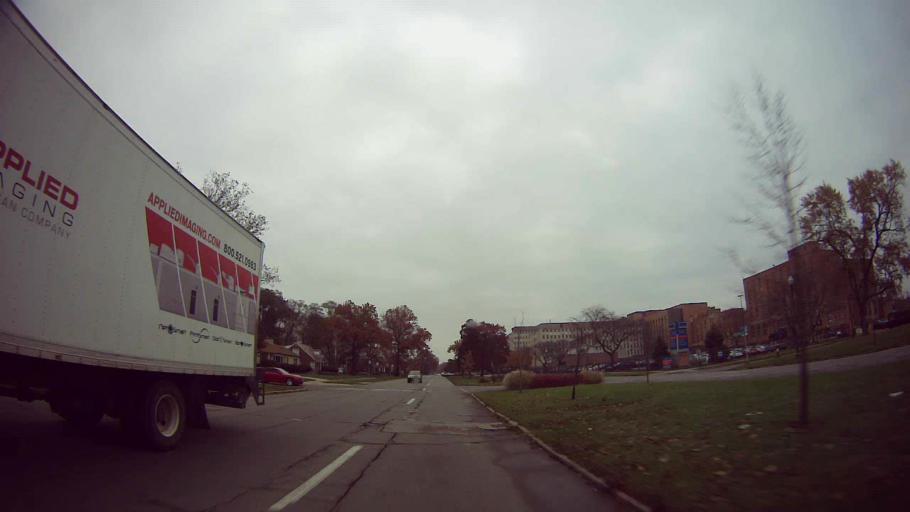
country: US
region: Michigan
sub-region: Oakland County
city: Oak Park
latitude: 42.4202
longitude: -83.1853
